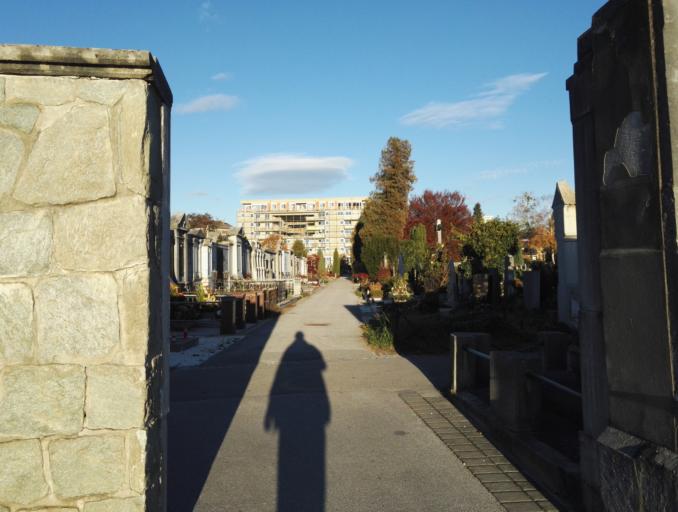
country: AT
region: Styria
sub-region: Graz Stadt
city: Graz
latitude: 47.0634
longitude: 15.4621
